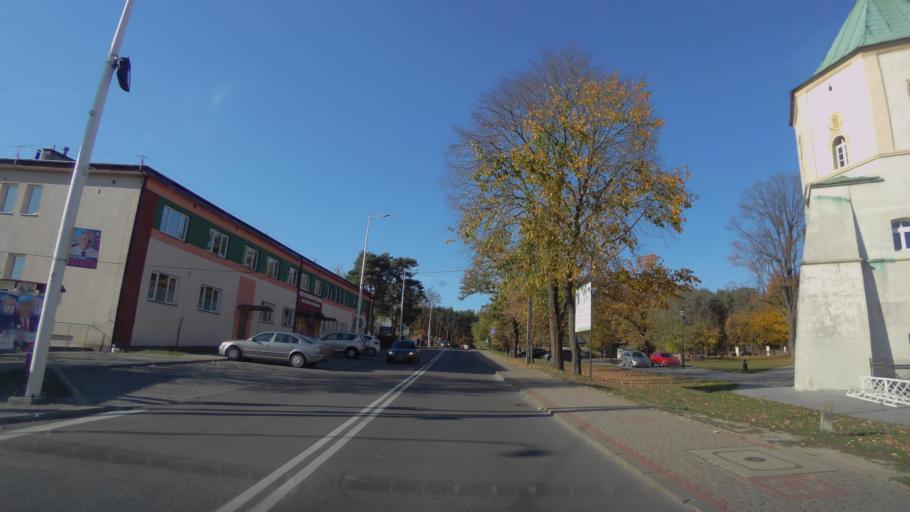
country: PL
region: Subcarpathian Voivodeship
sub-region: Powiat lezajski
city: Lezajsk
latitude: 50.2696
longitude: 22.4078
